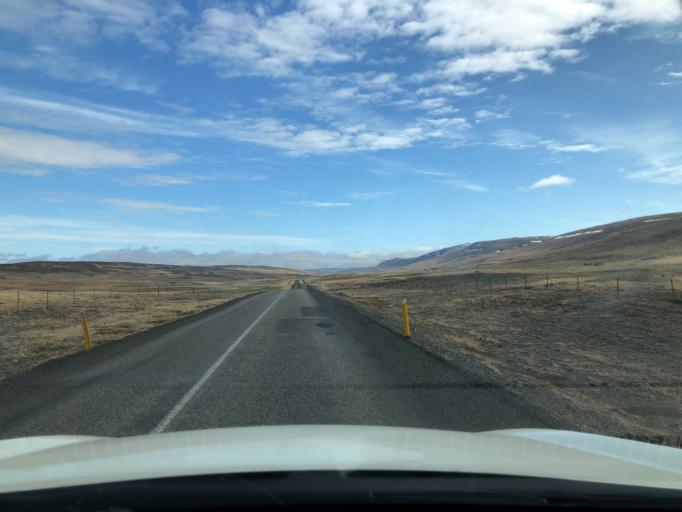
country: IS
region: West
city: Borgarnes
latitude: 65.1140
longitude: -21.6835
